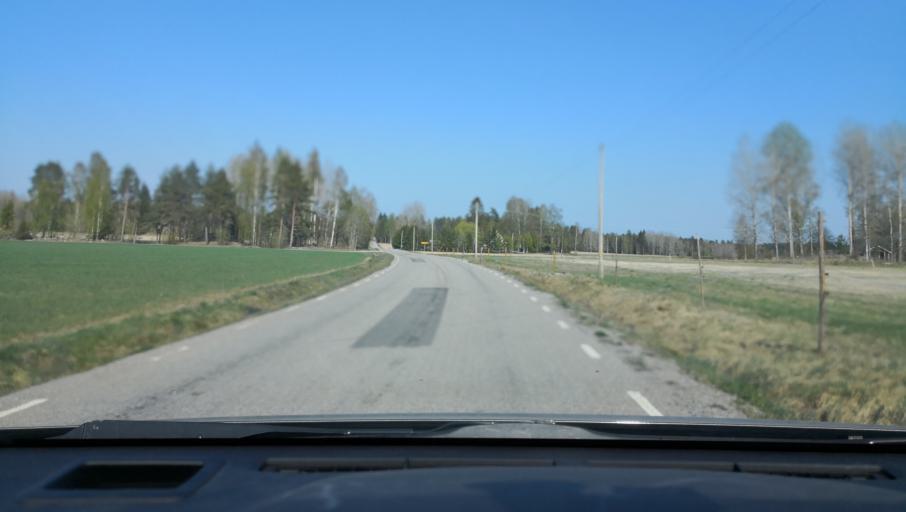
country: SE
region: Uppsala
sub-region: Heby Kommun
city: Heby
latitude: 60.0383
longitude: 16.8284
